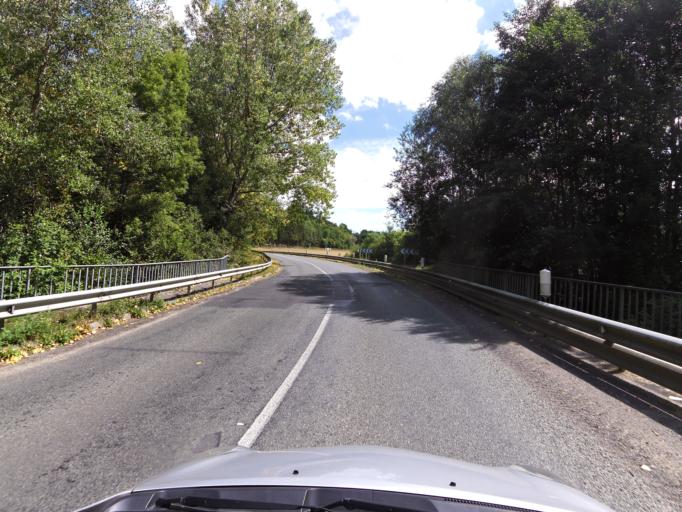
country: FR
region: Picardie
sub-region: Departement de l'Oise
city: Mareuil-sur-Ourcq
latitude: 49.1482
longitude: 3.1050
